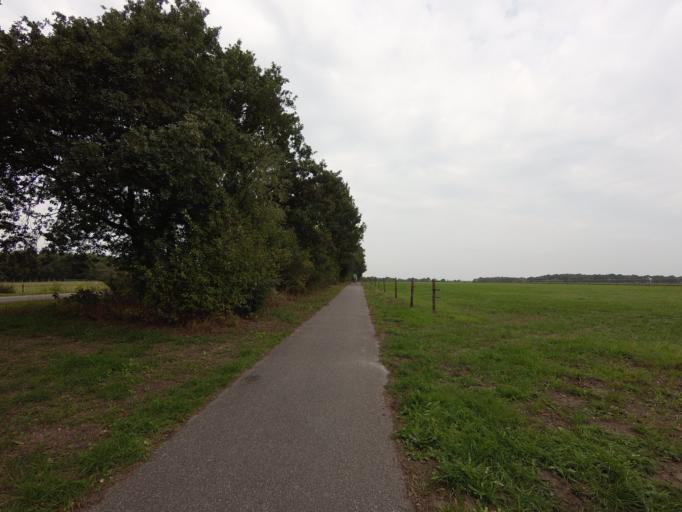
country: NL
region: Drenthe
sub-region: Gemeente Assen
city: Assen
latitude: 53.0008
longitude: 6.6348
